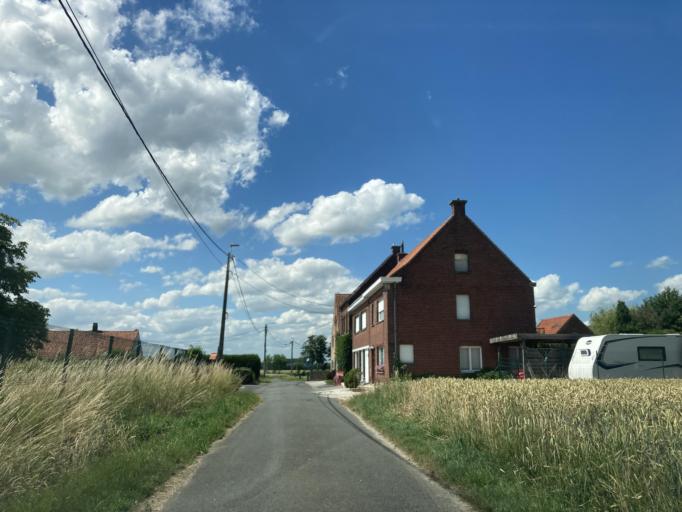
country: BE
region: Flanders
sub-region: Provincie West-Vlaanderen
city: Deerlijk
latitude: 50.8472
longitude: 3.3982
